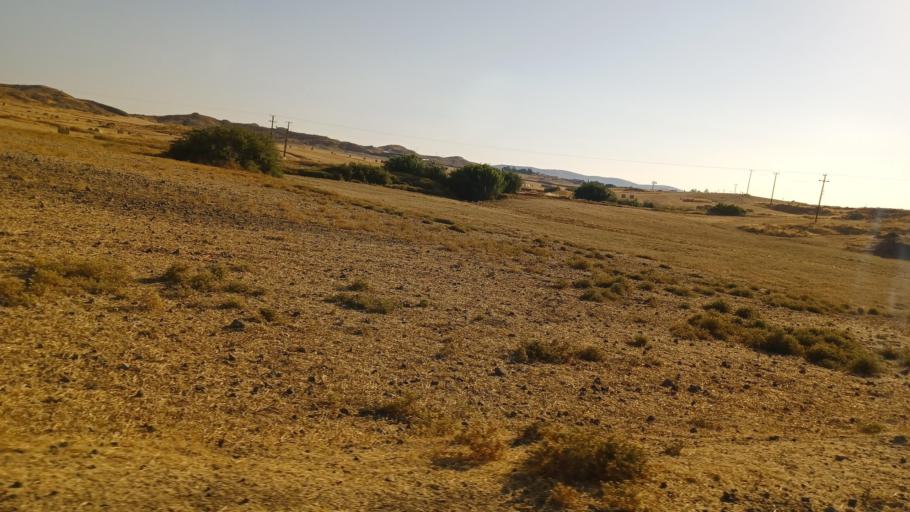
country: CY
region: Larnaka
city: Troulloi
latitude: 35.0120
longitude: 33.5992
